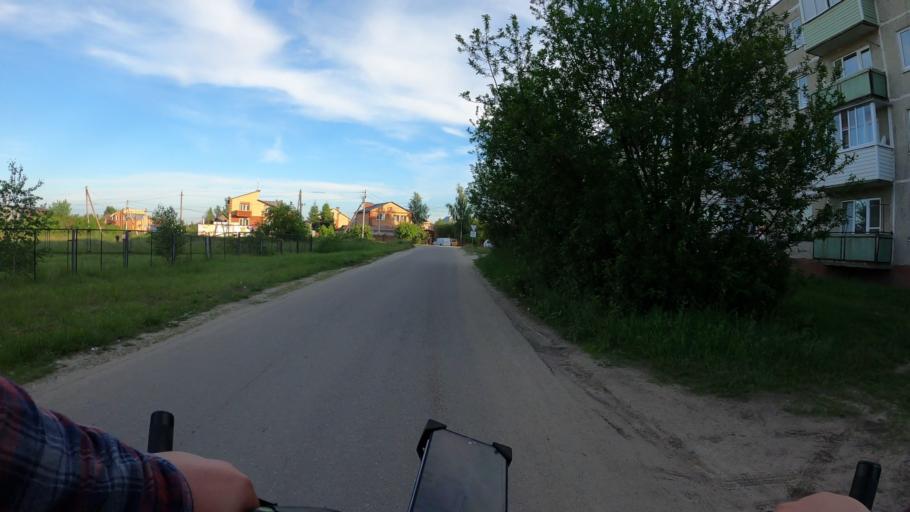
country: RU
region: Moskovskaya
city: Ashitkovo
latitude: 55.4352
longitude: 38.5834
